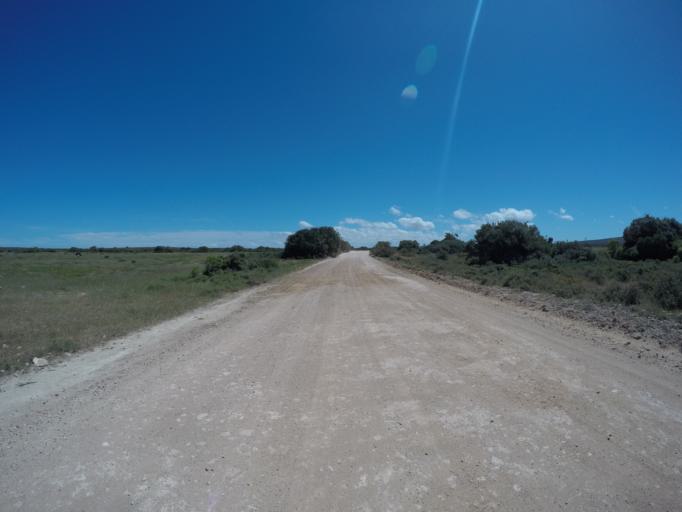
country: ZA
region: Western Cape
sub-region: Overberg District Municipality
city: Bredasdorp
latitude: -34.4546
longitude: 20.4227
